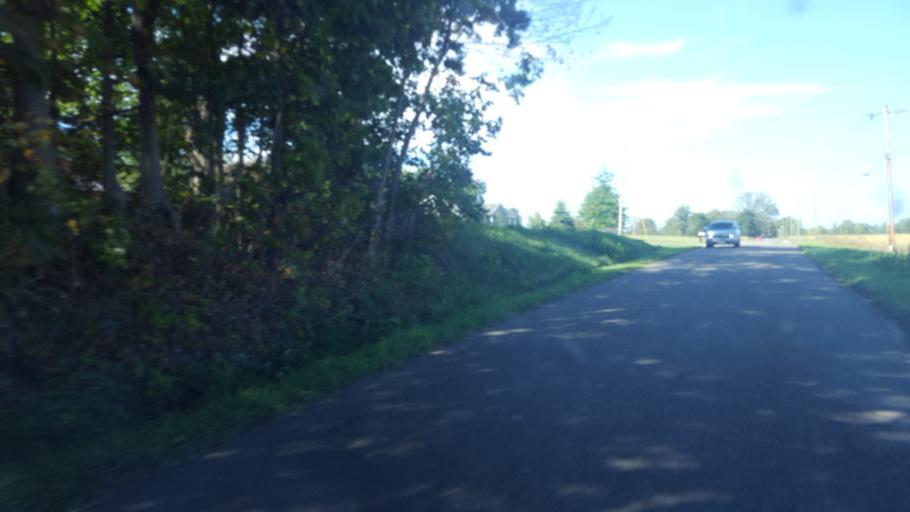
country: US
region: Ohio
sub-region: Morrow County
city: Mount Gilead
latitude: 40.5715
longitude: -82.7317
